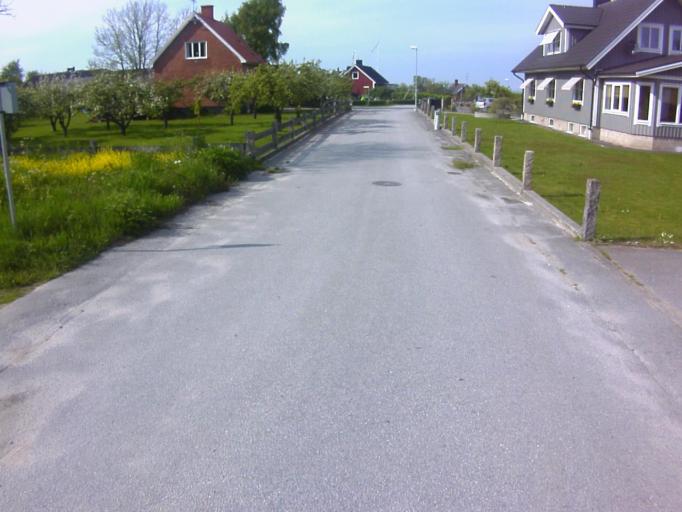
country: SE
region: Blekinge
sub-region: Karlshamns Kommun
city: Morrum
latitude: 56.0383
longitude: 14.7751
